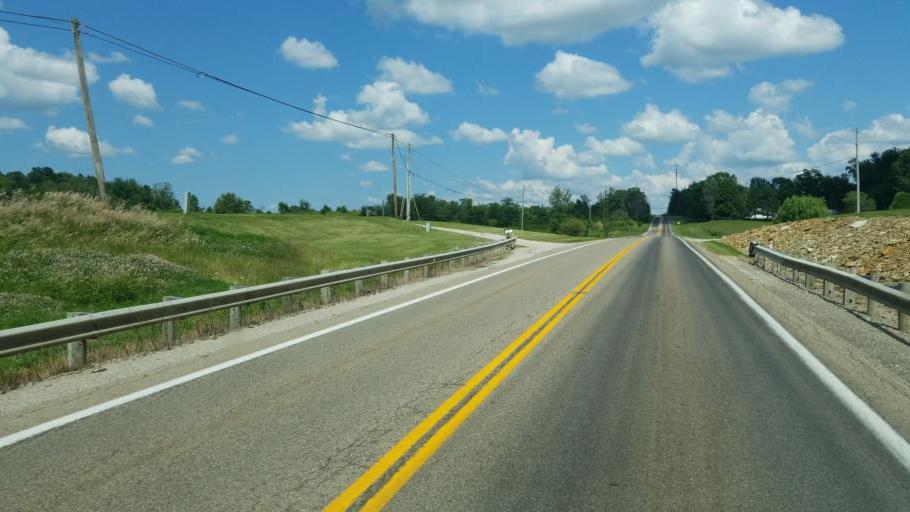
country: US
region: Ohio
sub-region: Crawford County
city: Galion
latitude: 40.6731
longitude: -82.8356
